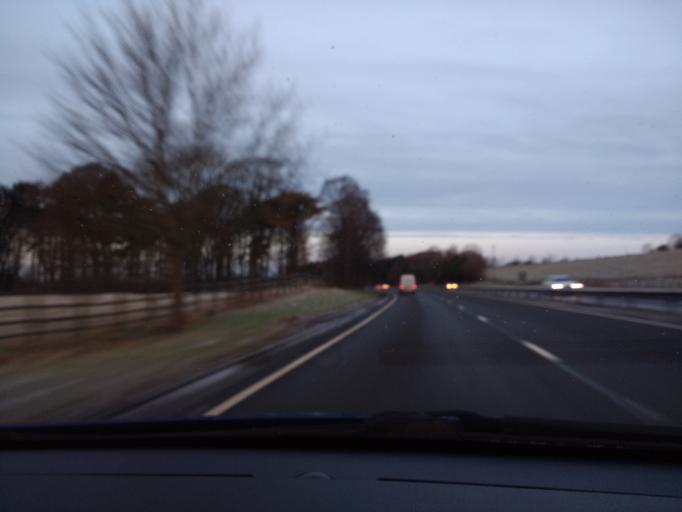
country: GB
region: England
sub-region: Northumberland
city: Corbridge
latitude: 54.9815
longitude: -1.9929
